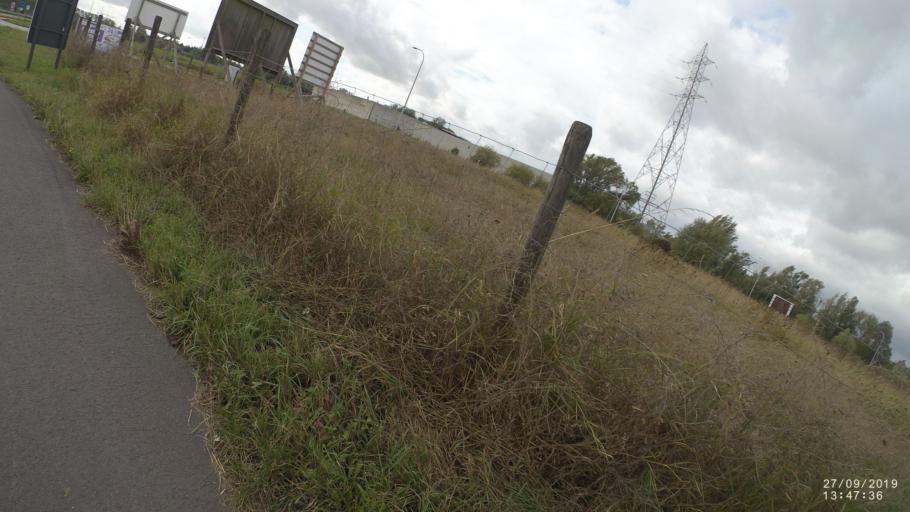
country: BE
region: Flanders
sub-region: Provincie Oost-Vlaanderen
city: Oudenaarde
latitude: 50.8556
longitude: 3.6236
